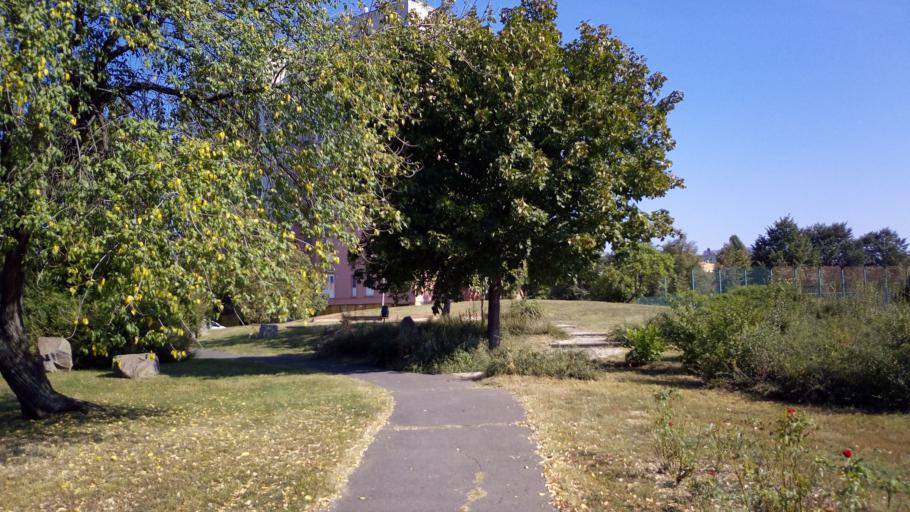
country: HU
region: Baranya
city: Pecs
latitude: 46.0641
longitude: 18.2029
